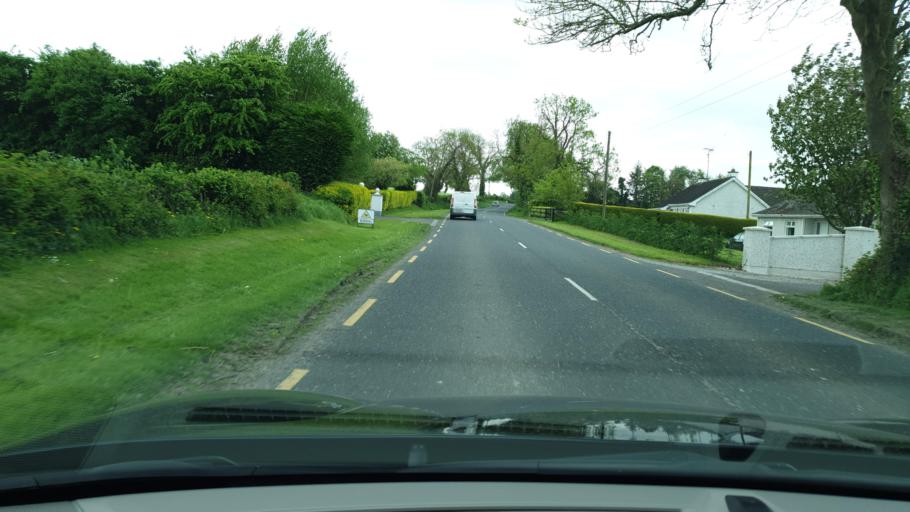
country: IE
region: Leinster
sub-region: An Mhi
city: Navan
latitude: 53.6900
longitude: -6.6737
